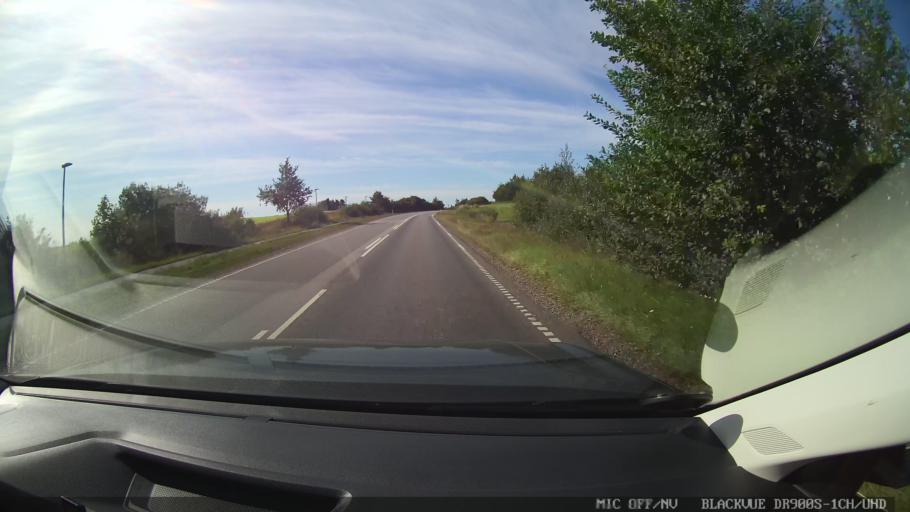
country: DK
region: North Denmark
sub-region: Mariagerfjord Kommune
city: Hobro
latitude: 56.6595
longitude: 9.8234
